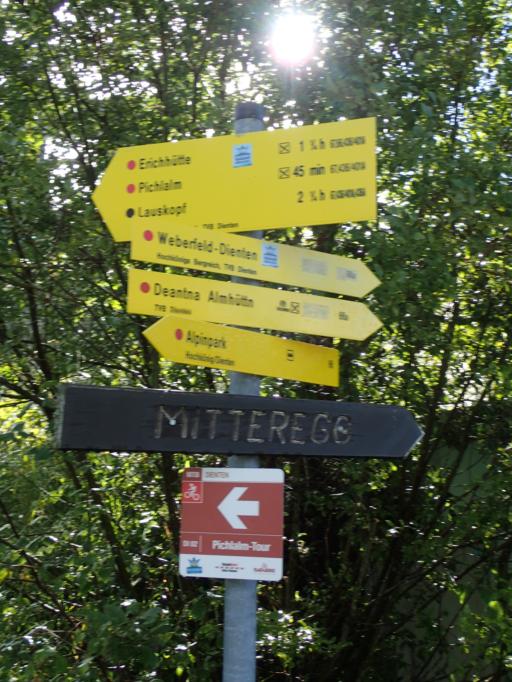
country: AT
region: Salzburg
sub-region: Politischer Bezirk Zell am See
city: Dienten am Hochkonig
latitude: 47.3939
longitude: 13.0171
